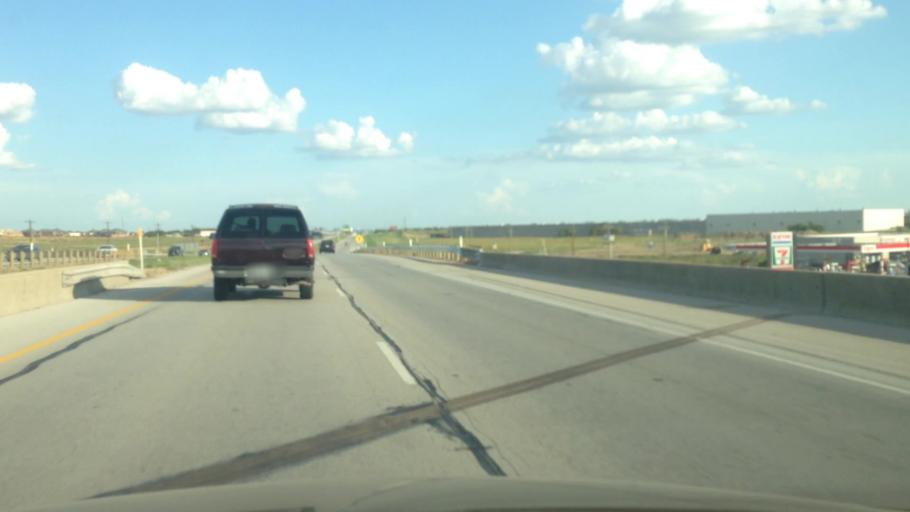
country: US
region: Texas
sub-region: Tarrant County
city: Saginaw
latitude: 32.9156
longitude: -97.3486
